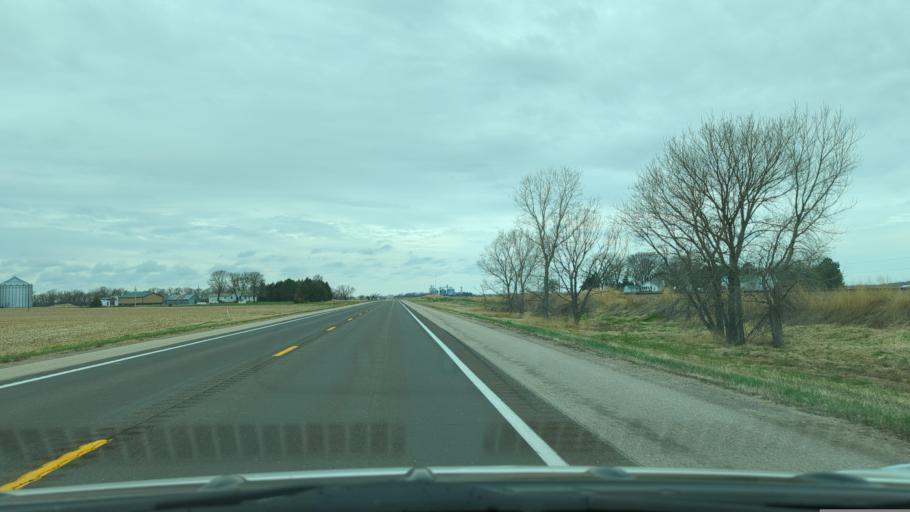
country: US
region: Nebraska
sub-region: Lancaster County
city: Waverly
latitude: 40.9383
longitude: -96.4846
